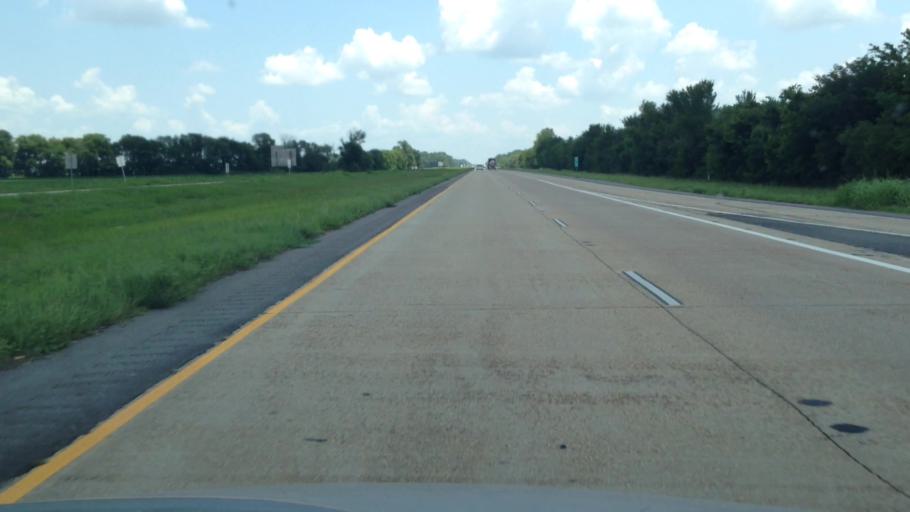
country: US
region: Louisiana
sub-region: Rapides Parish
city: Lecompte
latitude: 31.0127
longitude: -92.3717
